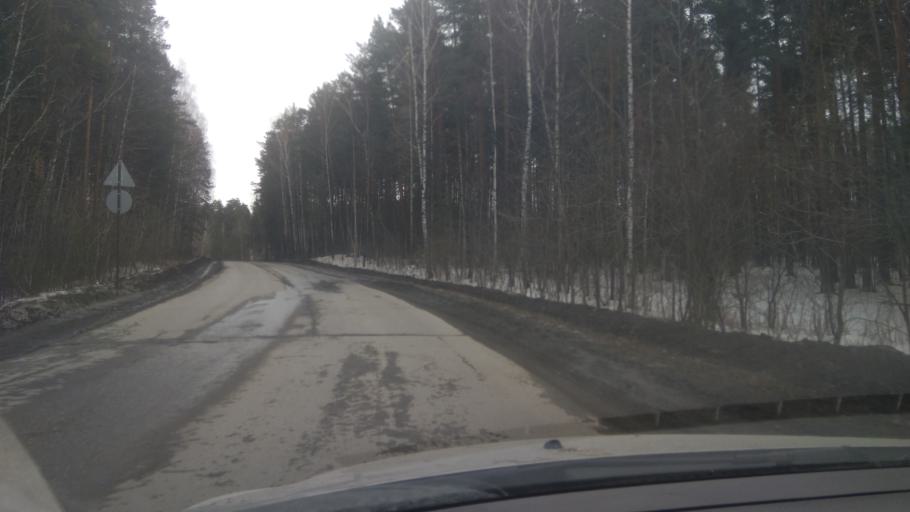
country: RU
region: Sverdlovsk
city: Severka
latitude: 56.8349
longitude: 60.3826
